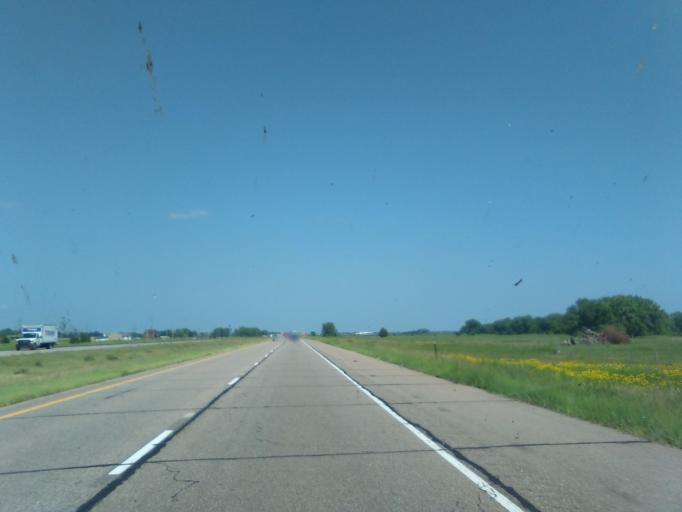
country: US
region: Nebraska
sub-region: Buffalo County
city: Kearney
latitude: 40.6701
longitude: -99.1382
